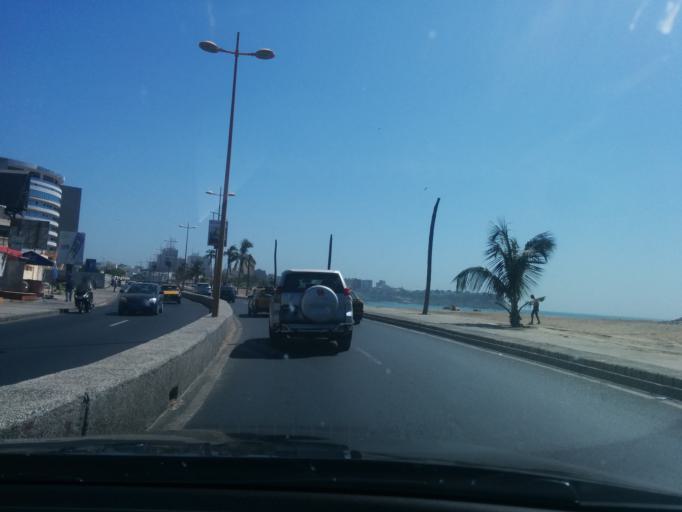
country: SN
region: Dakar
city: Dakar
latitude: 14.6747
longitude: -17.4528
